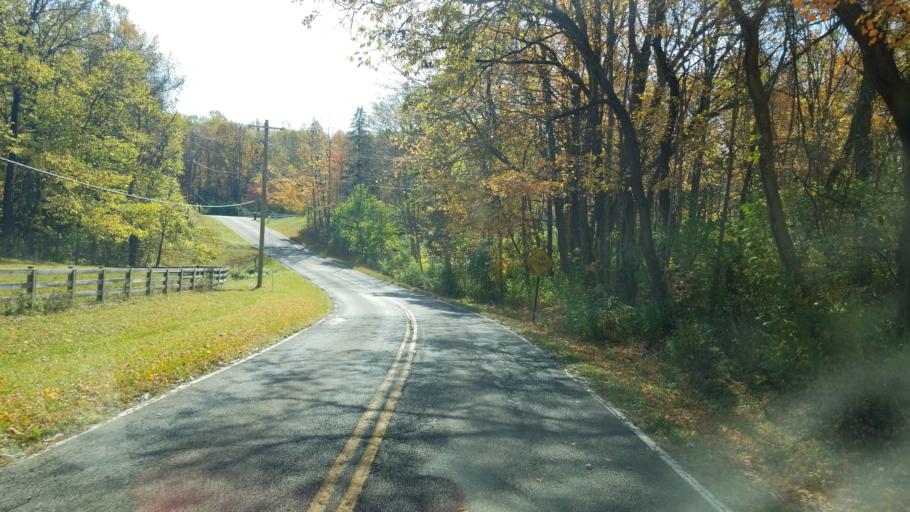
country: US
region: Ohio
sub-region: Warren County
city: Morrow
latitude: 39.4207
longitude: -84.0853
